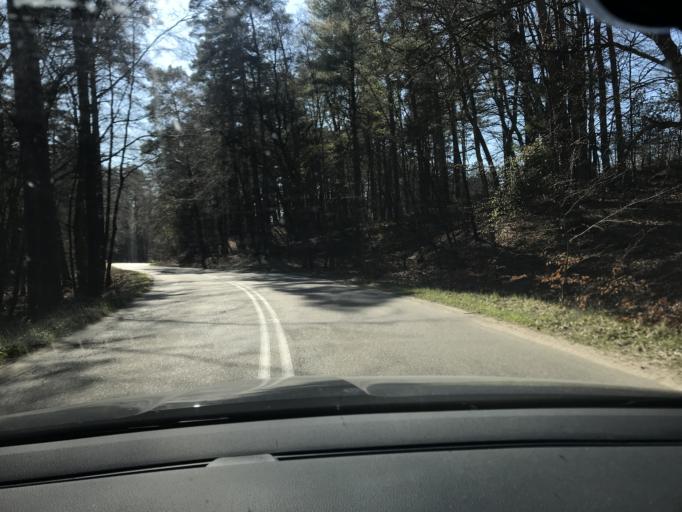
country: PL
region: Pomeranian Voivodeship
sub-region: Powiat nowodworski
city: Krynica Morska
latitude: 54.3640
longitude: 19.3632
